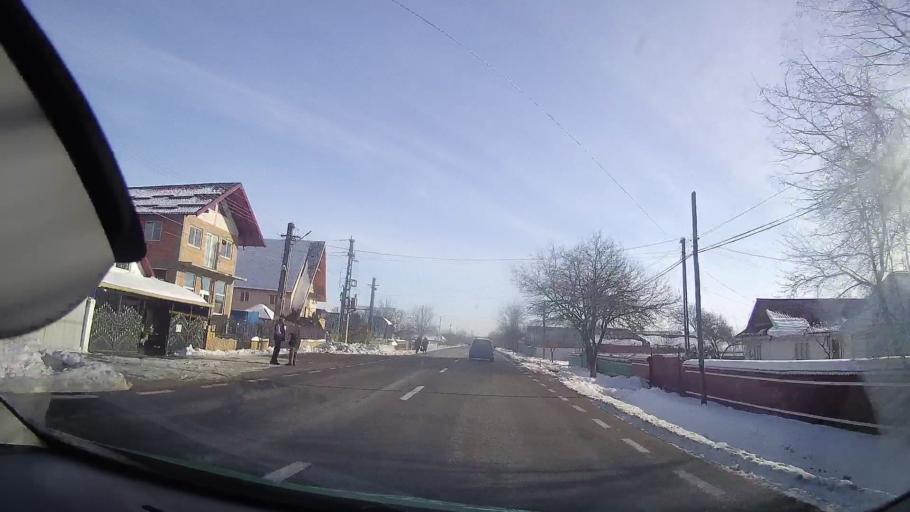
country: RO
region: Neamt
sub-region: Comuna Negresti
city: Negresti
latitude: 47.0555
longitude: 26.3952
